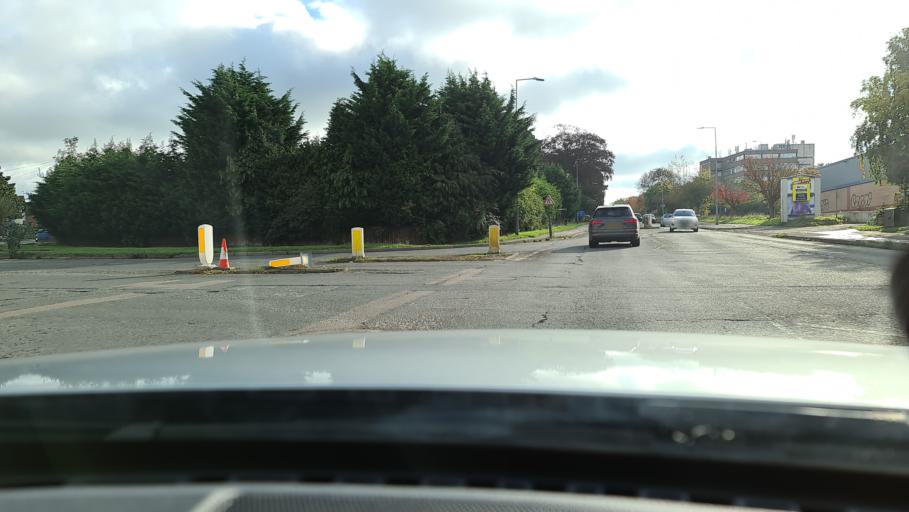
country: GB
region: England
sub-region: Milton Keynes
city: Water Eaton
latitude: 52.0012
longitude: -0.7226
